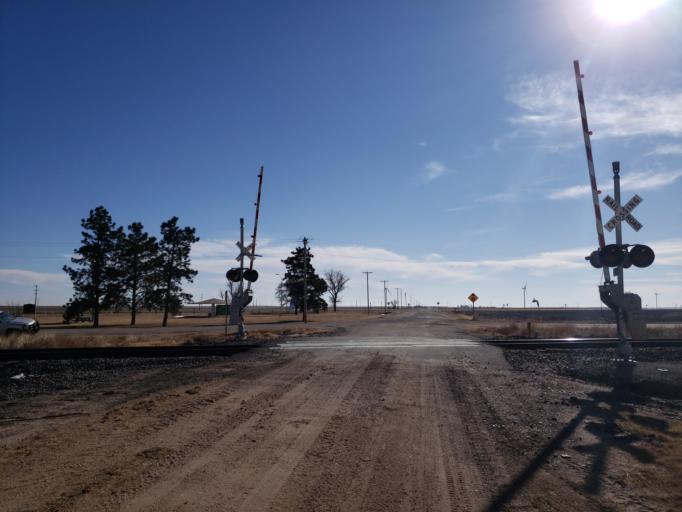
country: US
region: Kansas
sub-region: Ford County
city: Dodge City
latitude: 37.4916
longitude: -99.8882
